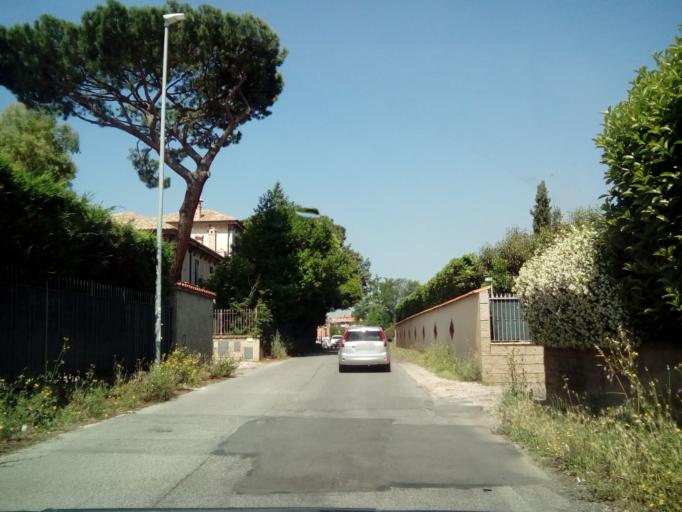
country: IT
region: Latium
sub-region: Citta metropolitana di Roma Capitale
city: Rome
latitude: 41.8761
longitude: 12.5879
